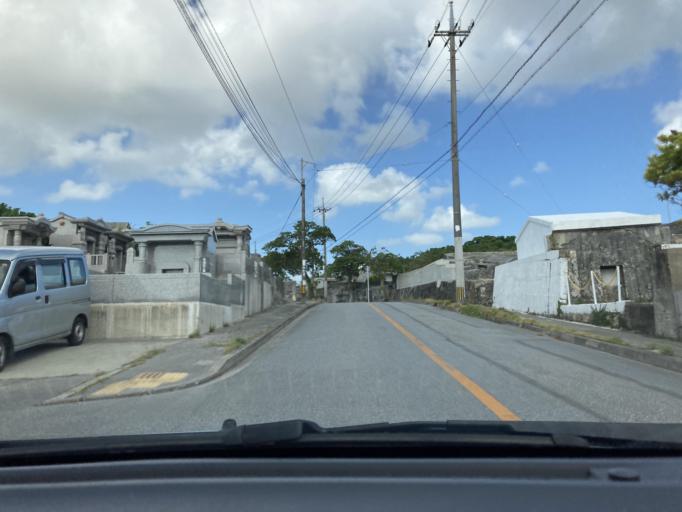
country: JP
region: Okinawa
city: Naha-shi
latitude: 26.2075
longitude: 127.7109
